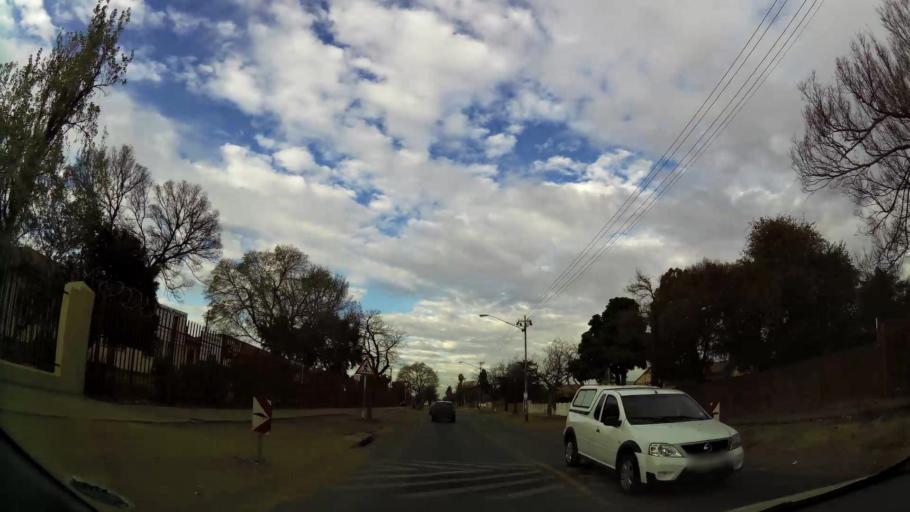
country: ZA
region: Gauteng
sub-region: City of Tshwane Metropolitan Municipality
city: Pretoria
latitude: -25.7151
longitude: 28.3116
